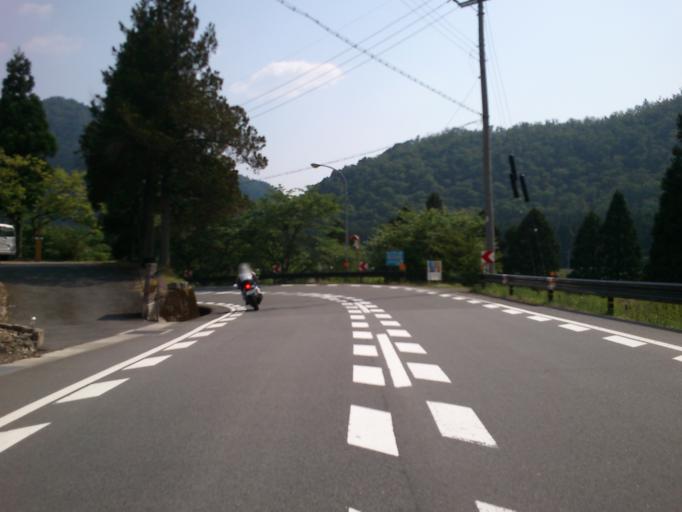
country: JP
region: Kyoto
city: Kameoka
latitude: 35.2652
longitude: 135.5717
